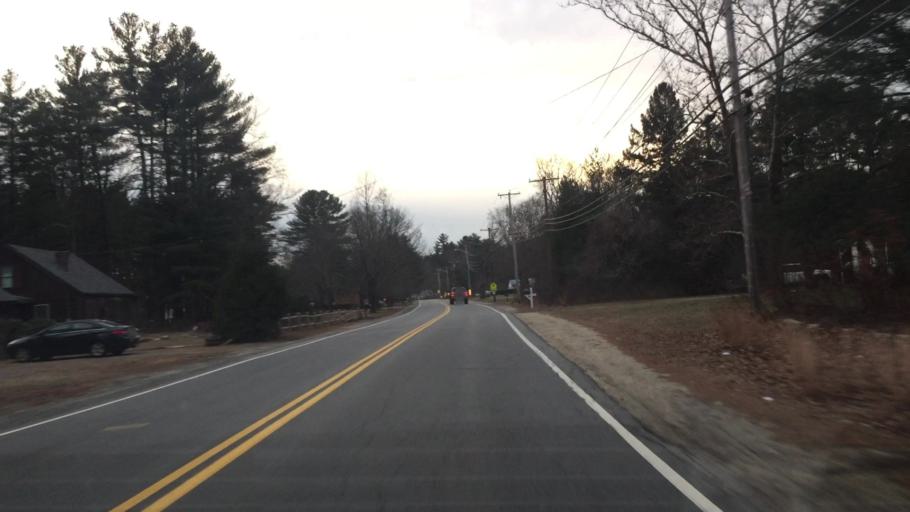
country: US
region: New Hampshire
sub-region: Hillsborough County
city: Pelham
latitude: 42.7261
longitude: -71.3295
